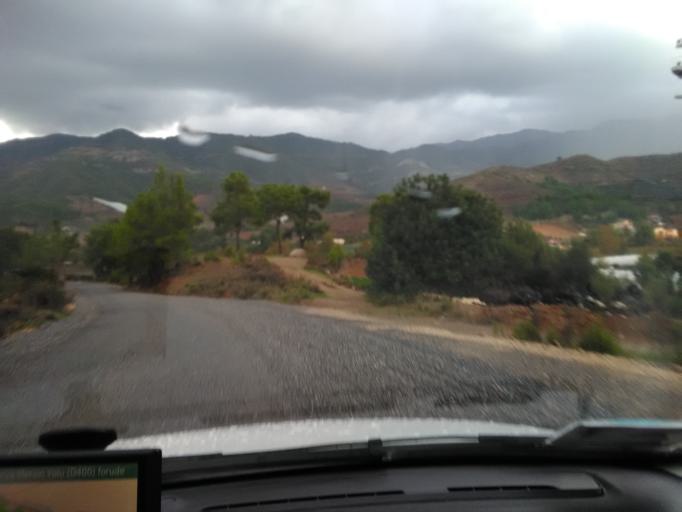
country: TR
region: Antalya
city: Gazipasa
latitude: 36.1668
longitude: 32.4442
